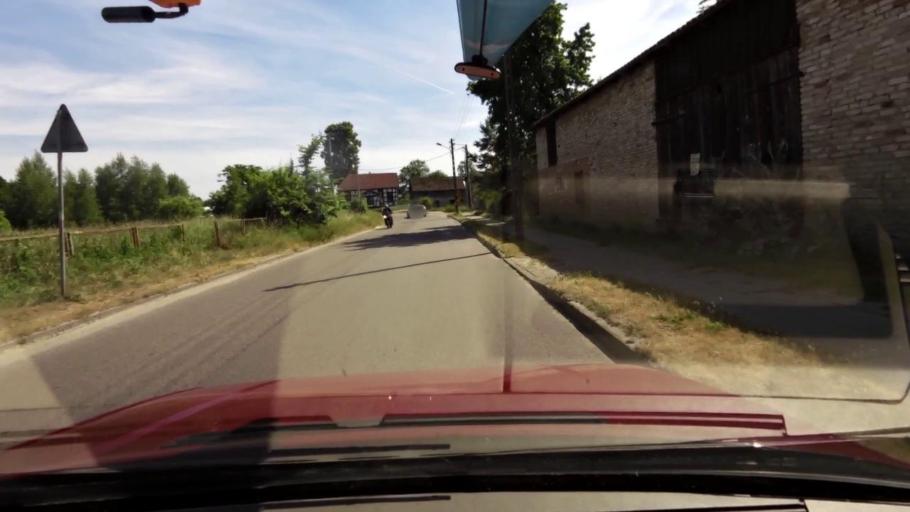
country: PL
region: Pomeranian Voivodeship
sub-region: Powiat slupski
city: Kobylnica
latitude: 54.3546
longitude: 16.9680
